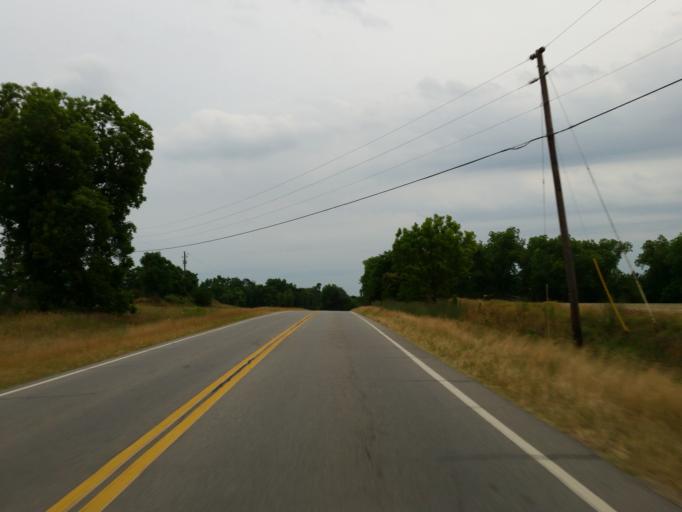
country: US
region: Georgia
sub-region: Dooly County
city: Vienna
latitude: 32.0641
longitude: -83.7983
